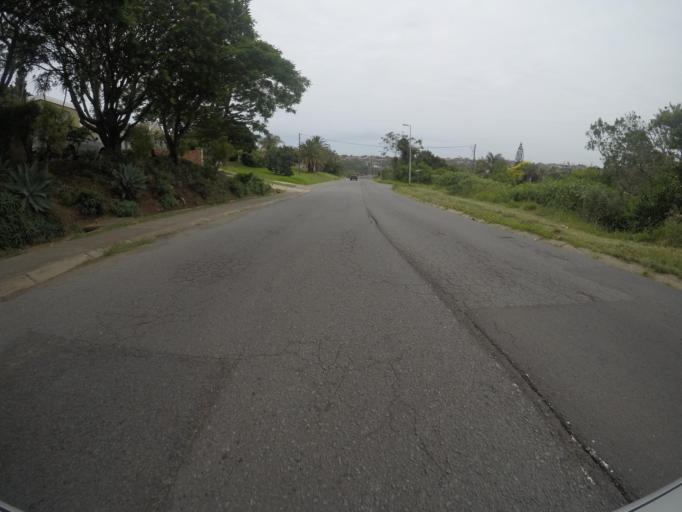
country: ZA
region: Eastern Cape
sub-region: Buffalo City Metropolitan Municipality
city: East London
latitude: -32.9780
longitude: 27.9404
